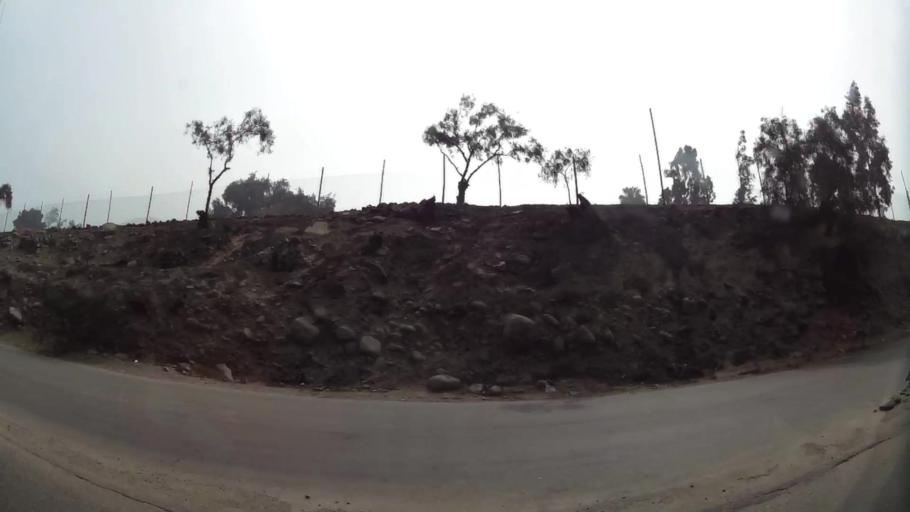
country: PE
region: Lima
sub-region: Lima
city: Chaclacayo
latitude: -11.9630
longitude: -76.7401
